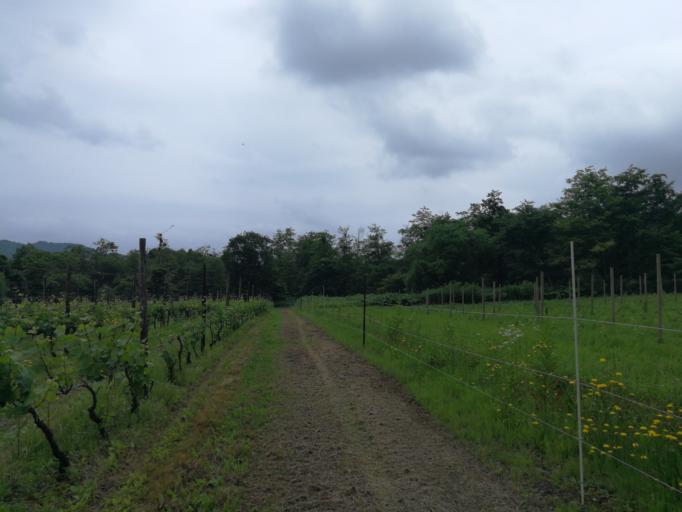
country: JP
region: Hokkaido
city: Iwamizawa
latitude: 43.1907
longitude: 141.8197
